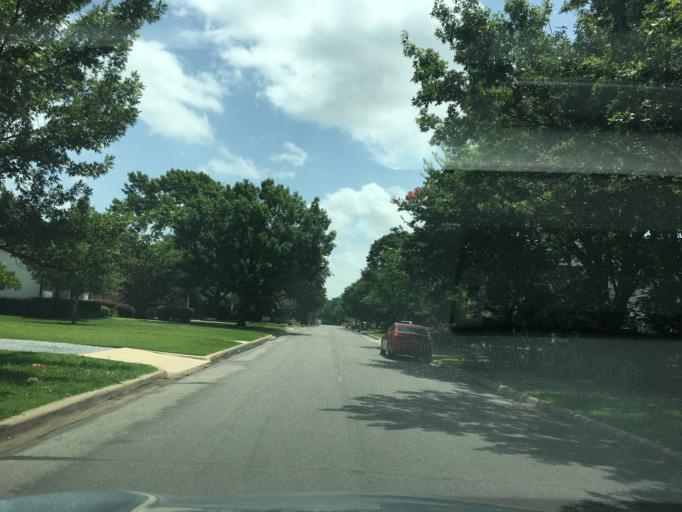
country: US
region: Texas
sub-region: Dallas County
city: University Park
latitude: 32.8926
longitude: -96.7959
